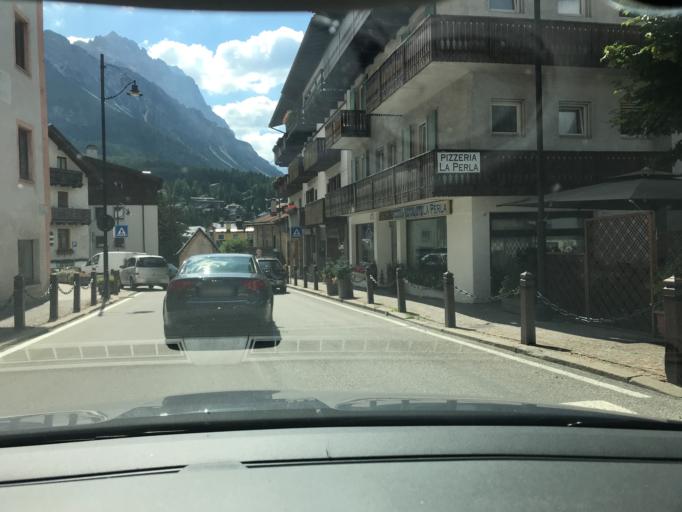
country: IT
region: Veneto
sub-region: Provincia di Belluno
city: Cortina d'Ampezzo
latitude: 46.5369
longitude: 12.1369
